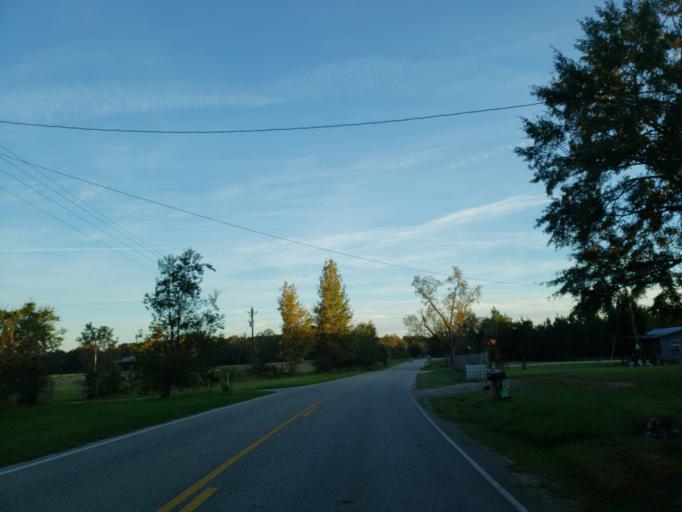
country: US
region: Mississippi
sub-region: Wayne County
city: Belmont
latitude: 31.4254
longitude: -88.4714
